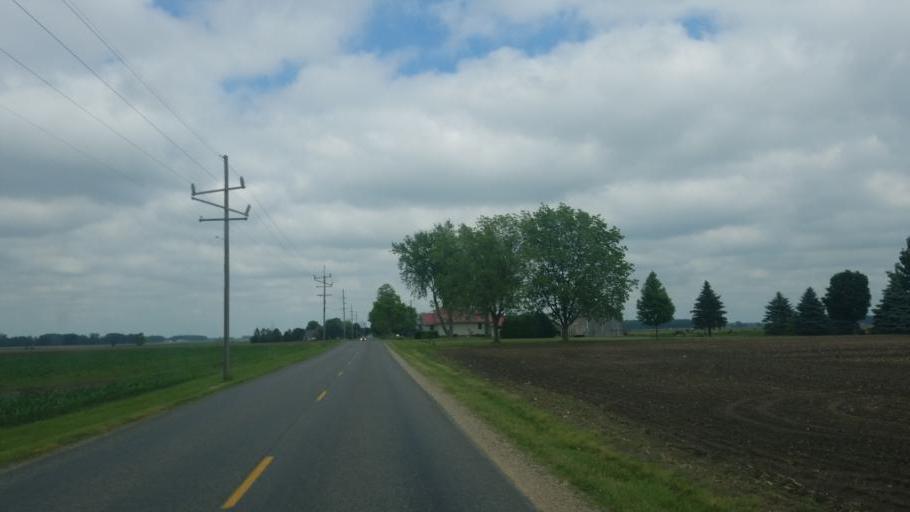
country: US
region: Indiana
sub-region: Elkhart County
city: Wakarusa
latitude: 41.4935
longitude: -86.0180
